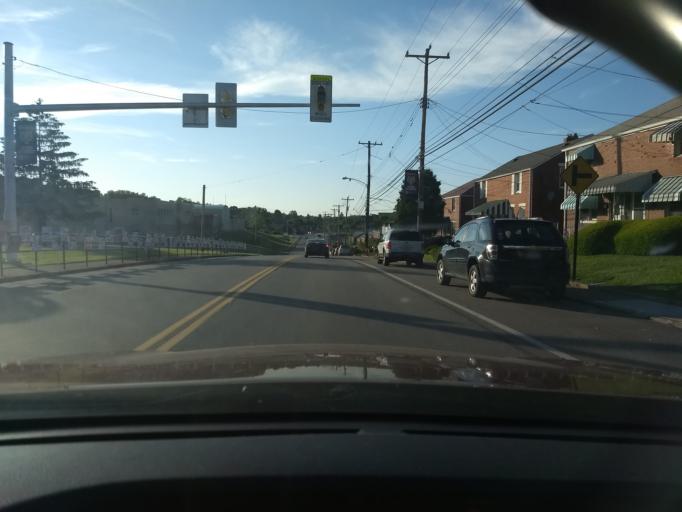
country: US
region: Pennsylvania
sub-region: Allegheny County
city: White Oak
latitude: 40.3453
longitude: -79.8307
